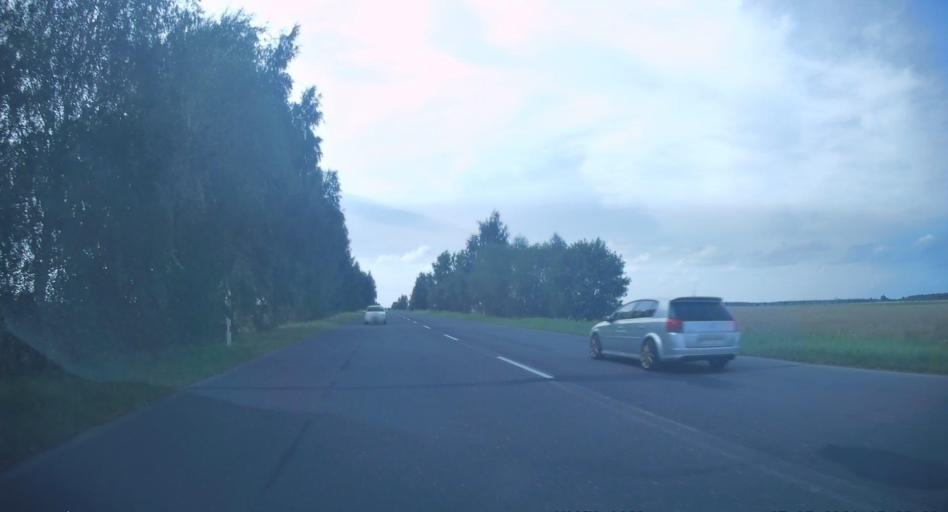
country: PL
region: Lodz Voivodeship
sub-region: Powiat tomaszowski
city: Rzeczyca
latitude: 51.6531
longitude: 20.2770
